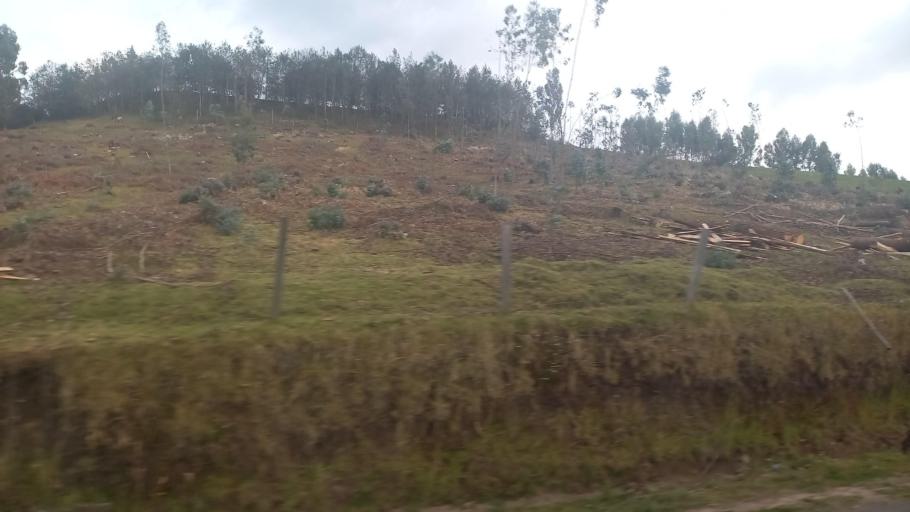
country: EC
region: Pichincha
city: Cayambe
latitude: 0.1014
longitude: -78.0863
